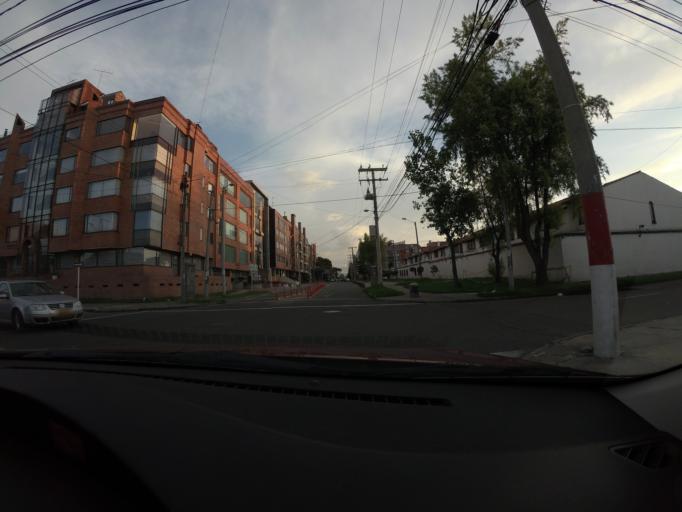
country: CO
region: Bogota D.C.
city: Barrio San Luis
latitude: 4.7067
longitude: -74.0584
